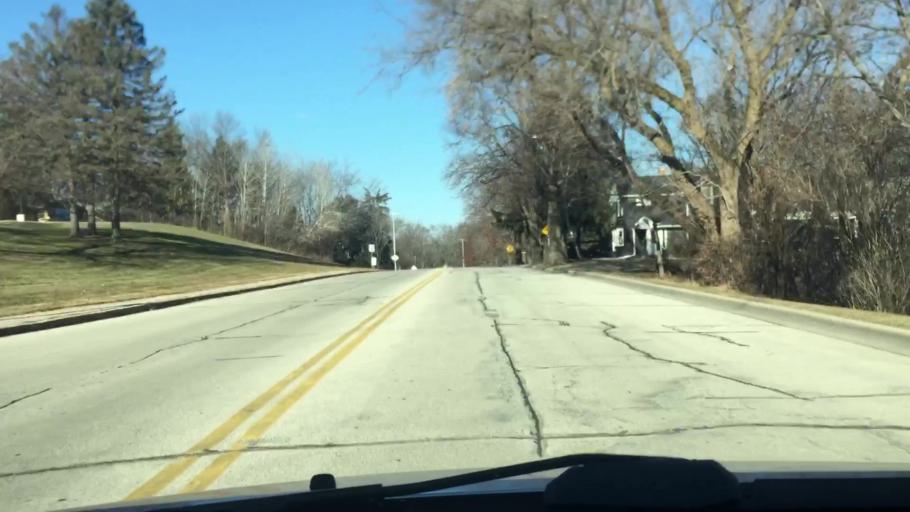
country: US
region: Wisconsin
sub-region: Waukesha County
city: Pewaukee
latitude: 43.0767
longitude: -88.2539
